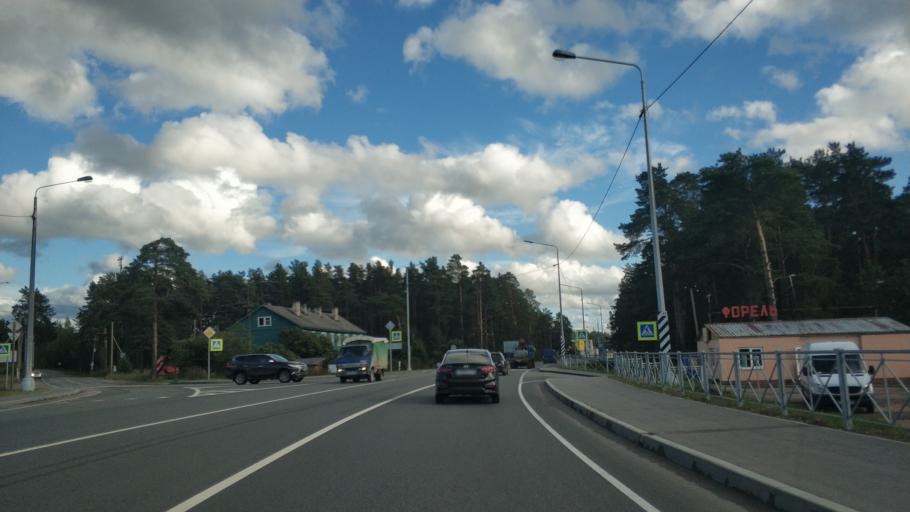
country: RU
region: Leningrad
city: Priozersk
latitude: 61.0056
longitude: 30.1789
